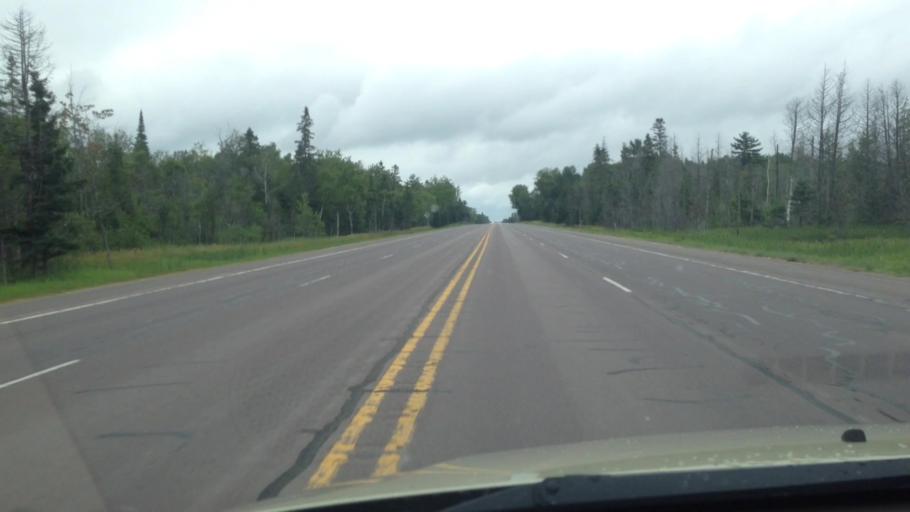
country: US
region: Michigan
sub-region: Schoolcraft County
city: Manistique
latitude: 46.0063
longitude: -85.9983
